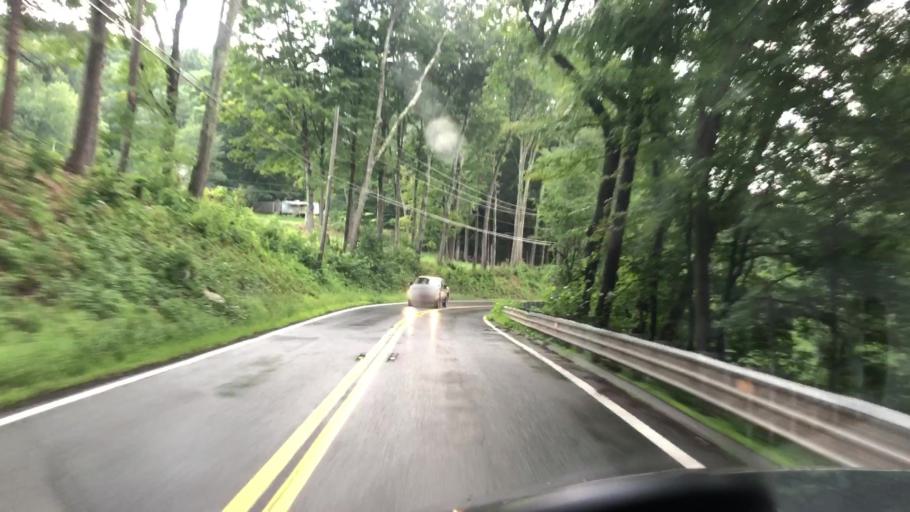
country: US
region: Massachusetts
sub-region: Hampshire County
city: Westhampton
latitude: 42.2597
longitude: -72.8638
